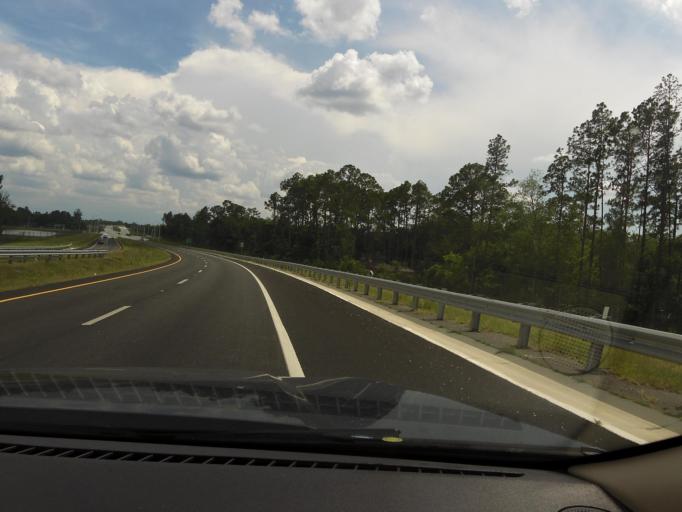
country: US
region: Florida
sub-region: Duval County
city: Baldwin
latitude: 30.3082
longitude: -81.9893
